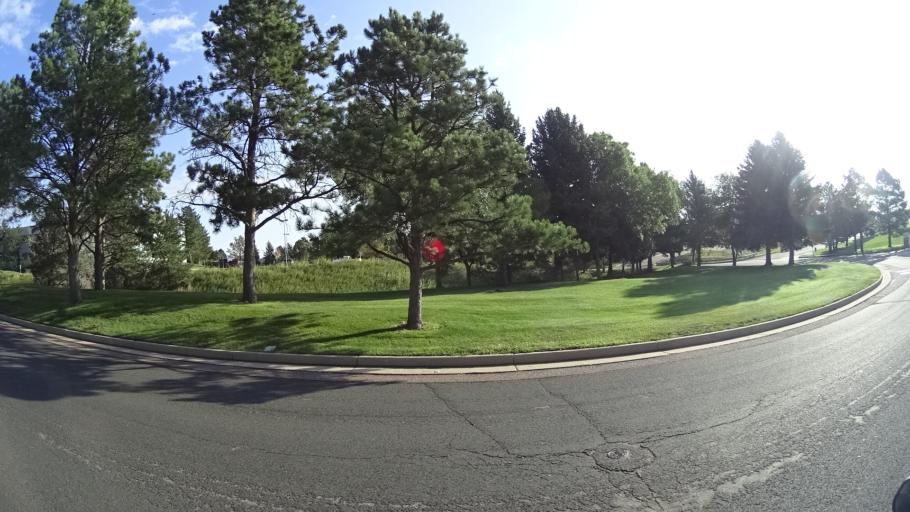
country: US
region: Colorado
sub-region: El Paso County
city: Manitou Springs
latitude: 38.8944
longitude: -104.8649
